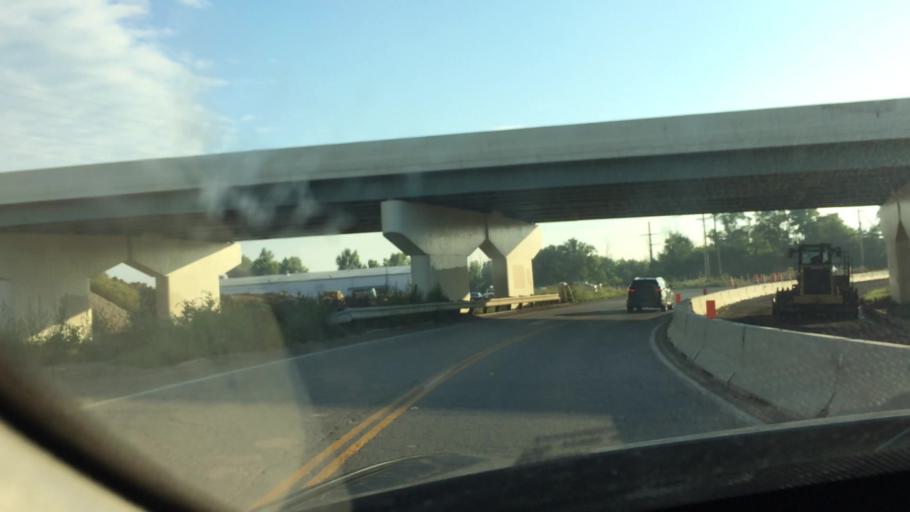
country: US
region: Ohio
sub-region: Hancock County
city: Findlay
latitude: 41.0237
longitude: -83.6689
